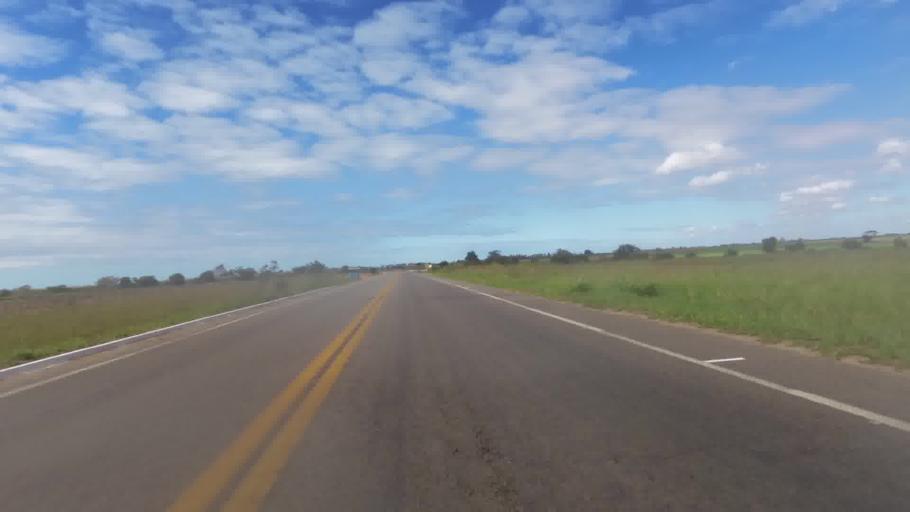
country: BR
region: Espirito Santo
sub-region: Marataizes
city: Marataizes
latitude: -21.0662
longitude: -40.8509
